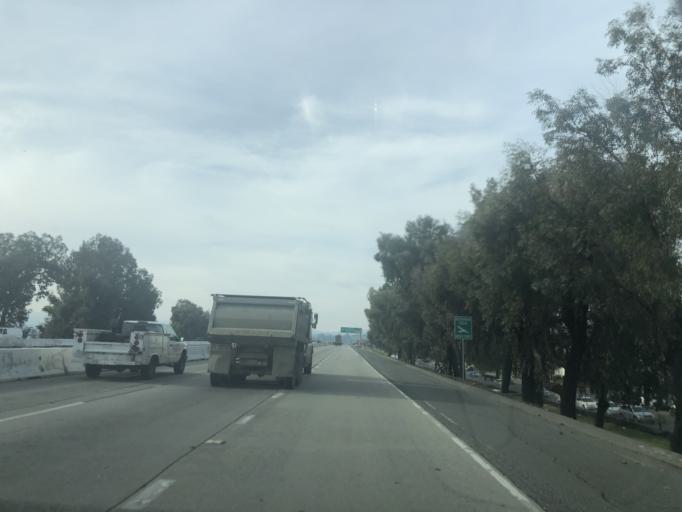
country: US
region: California
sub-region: Contra Costa County
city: Concord
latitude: 38.0035
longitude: -122.0440
